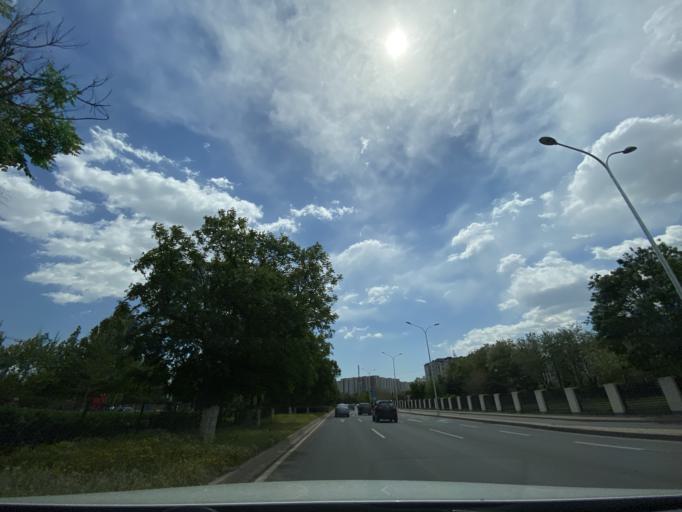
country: CN
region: Beijing
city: Sijiqing
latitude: 39.9348
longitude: 116.2443
